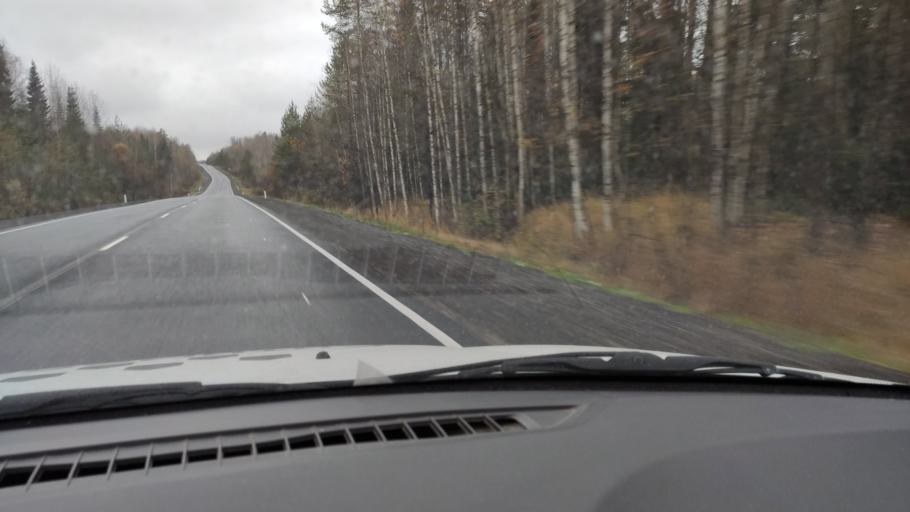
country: RU
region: Kirov
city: Chernaya Kholunitsa
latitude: 58.8718
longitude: 51.5282
